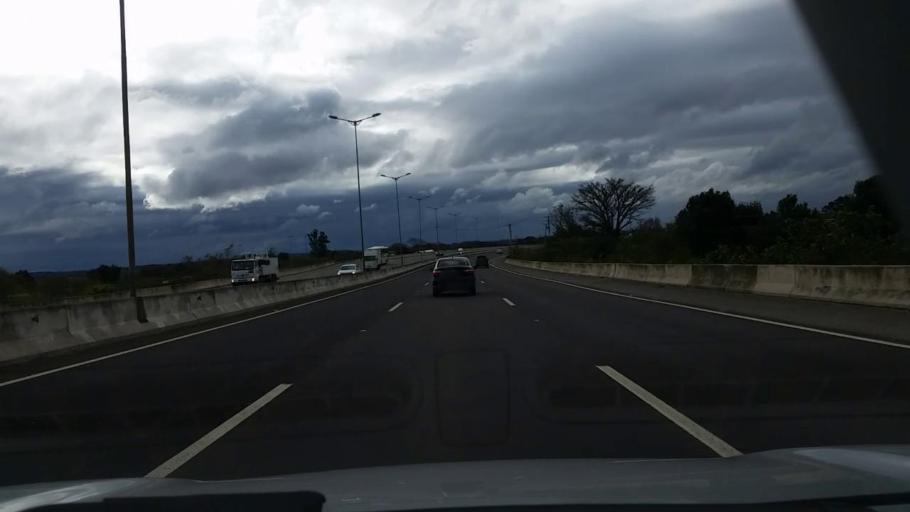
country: BR
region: Rio Grande do Sul
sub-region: Canoas
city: Canoas
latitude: -29.9655
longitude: -51.2021
